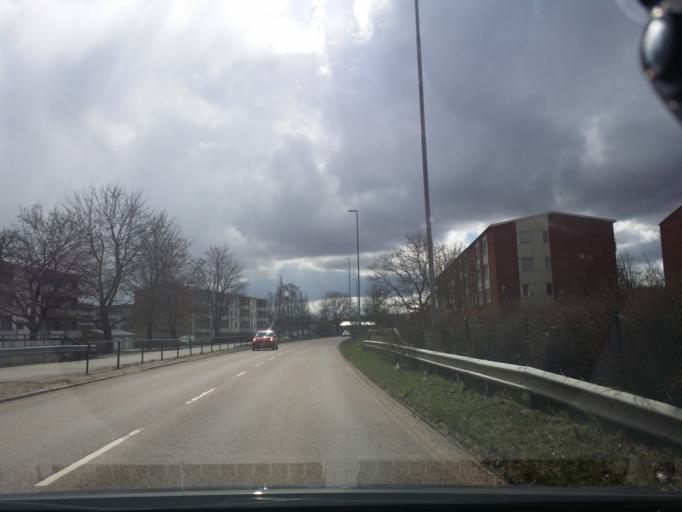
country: SE
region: Vaestmanland
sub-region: Sala Kommun
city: Sala
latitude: 59.9245
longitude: 16.5896
